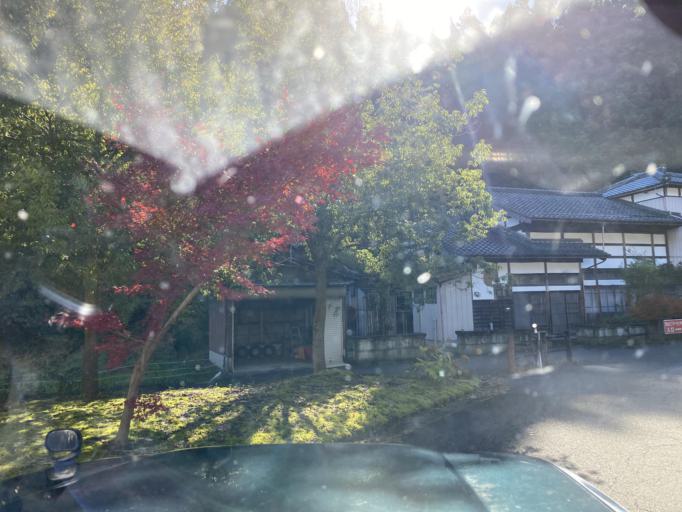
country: JP
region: Niigata
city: Niitsu-honcho
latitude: 37.7497
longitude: 139.1134
